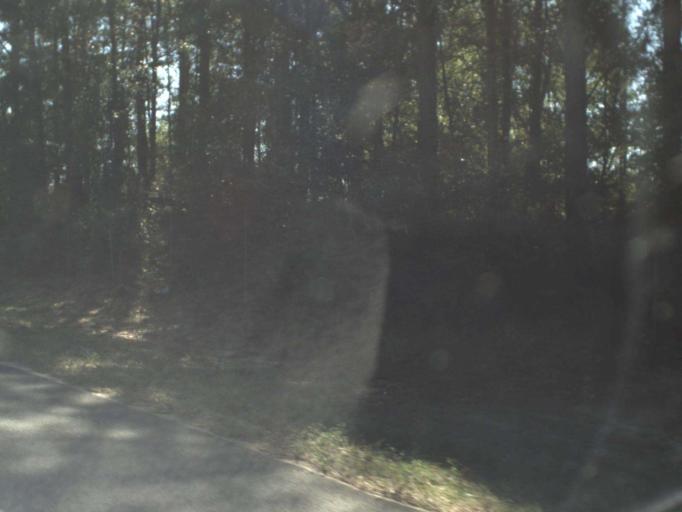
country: US
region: Florida
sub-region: Okaloosa County
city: Crestview
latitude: 30.7701
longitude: -86.6720
